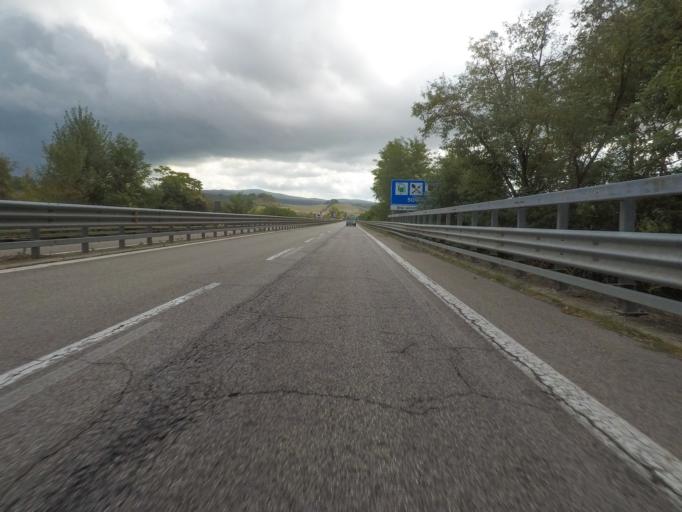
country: IT
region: Tuscany
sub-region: Provincia di Siena
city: Rapolano Terme
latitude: 43.3252
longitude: 11.5591
